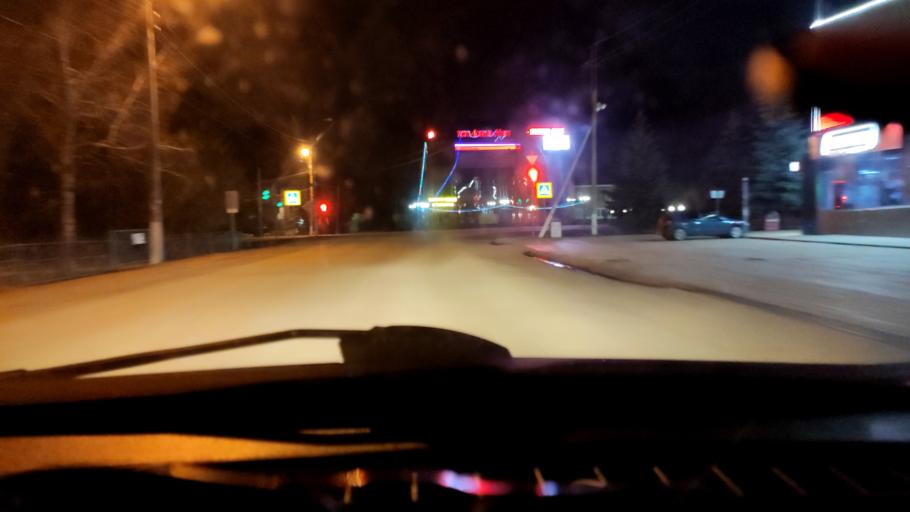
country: RU
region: Bashkortostan
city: Tolbazy
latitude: 54.0107
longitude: 55.8858
